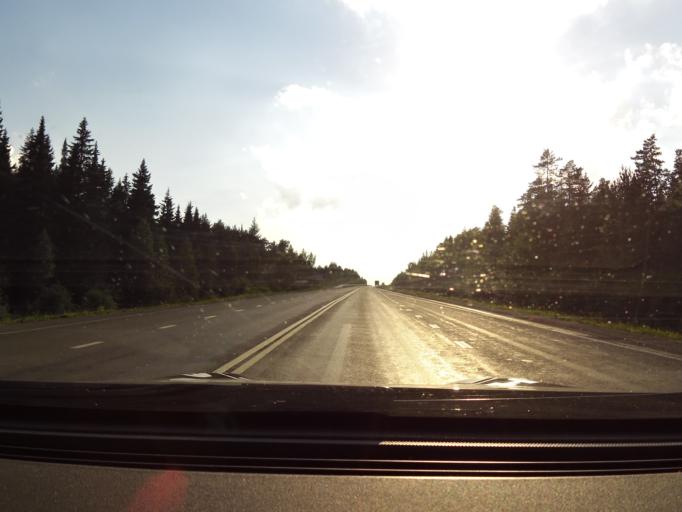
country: RU
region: Sverdlovsk
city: Revda
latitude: 56.8266
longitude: 59.9215
